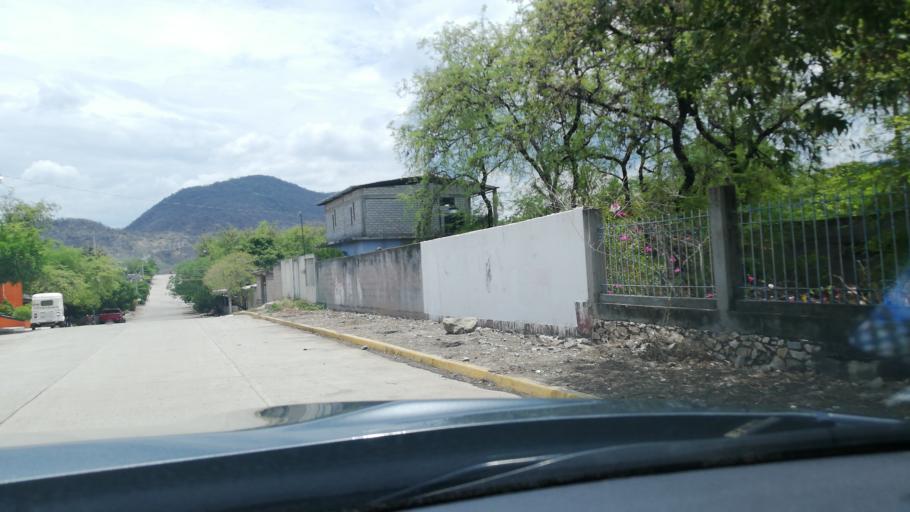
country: MX
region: Oaxaca
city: Santa Maria Jalapa del Marques
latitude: 16.4420
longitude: -95.4405
